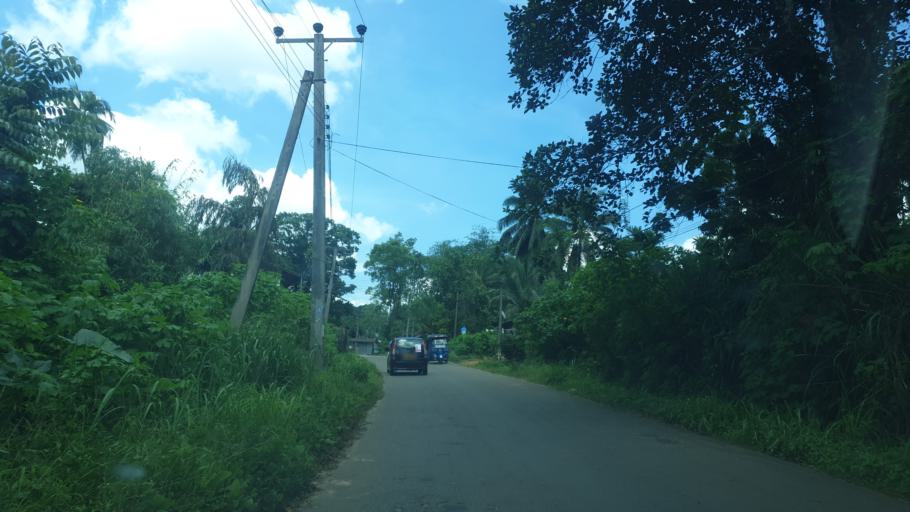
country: LK
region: Sabaragamuwa
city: Ratnapura
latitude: 6.4926
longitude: 80.3973
